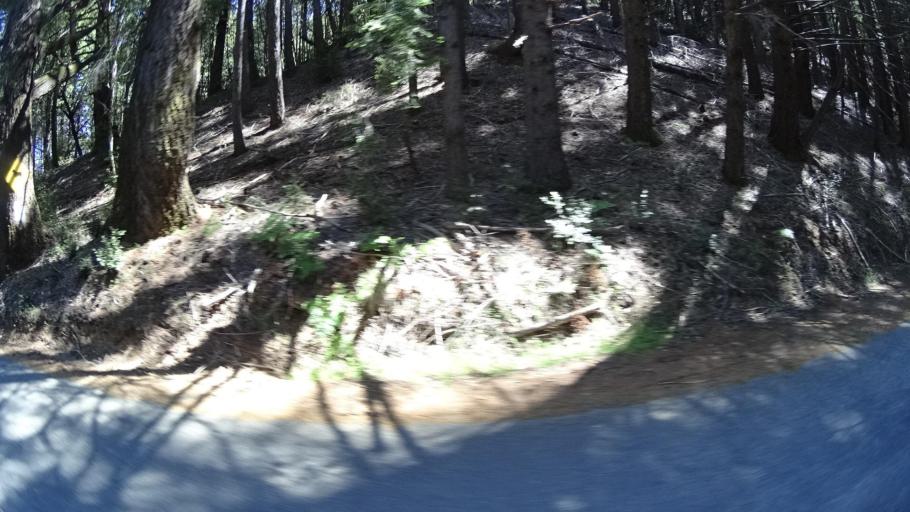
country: US
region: California
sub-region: Humboldt County
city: Redway
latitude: 40.1122
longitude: -123.9615
